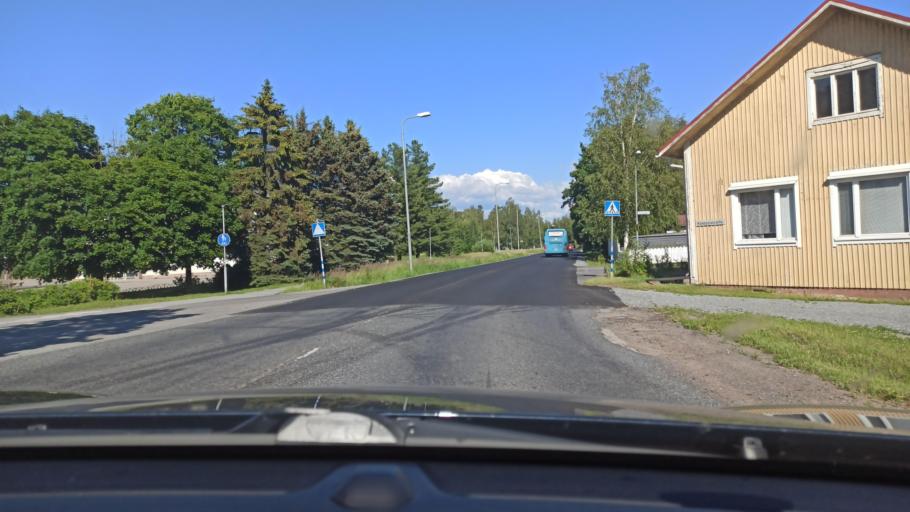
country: FI
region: Satakunta
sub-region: Pori
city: Pori
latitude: 61.4951
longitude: 21.8163
